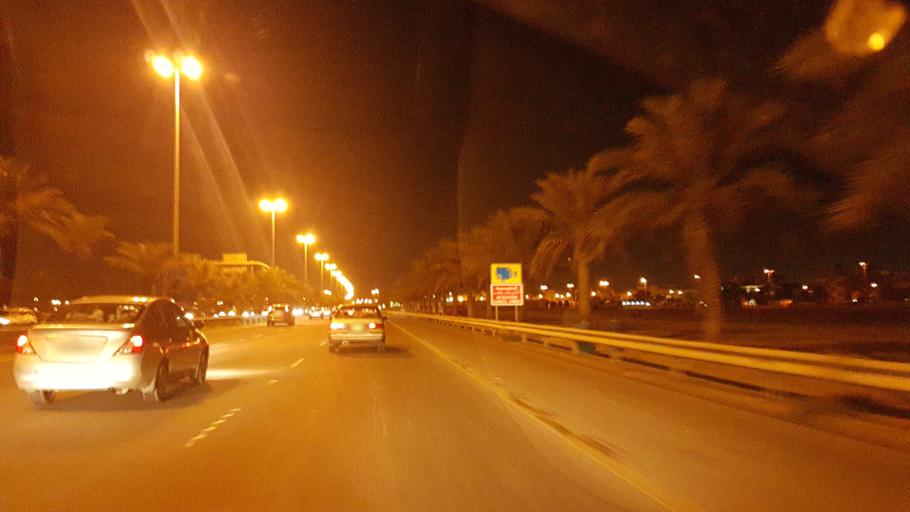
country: BH
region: Muharraq
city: Al Hadd
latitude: 26.2507
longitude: 50.6592
